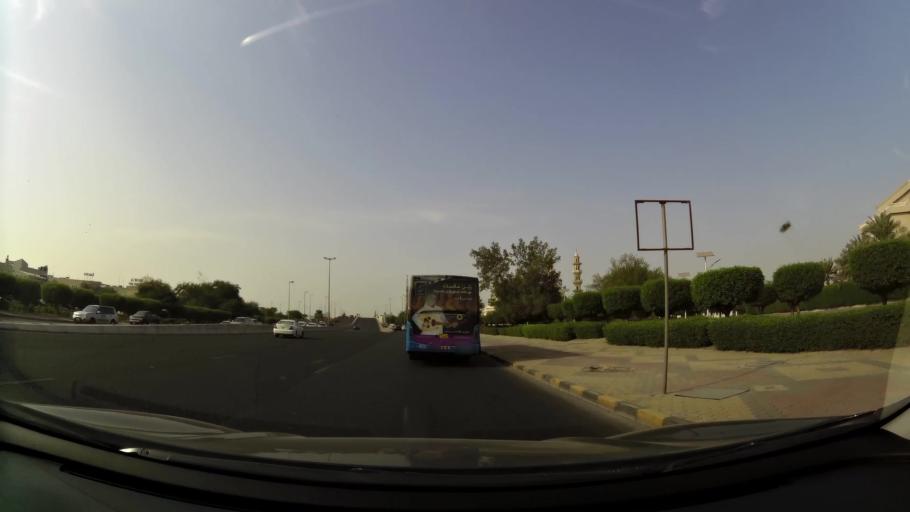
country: KW
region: Al Asimah
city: Ash Shamiyah
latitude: 29.3311
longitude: 47.9541
